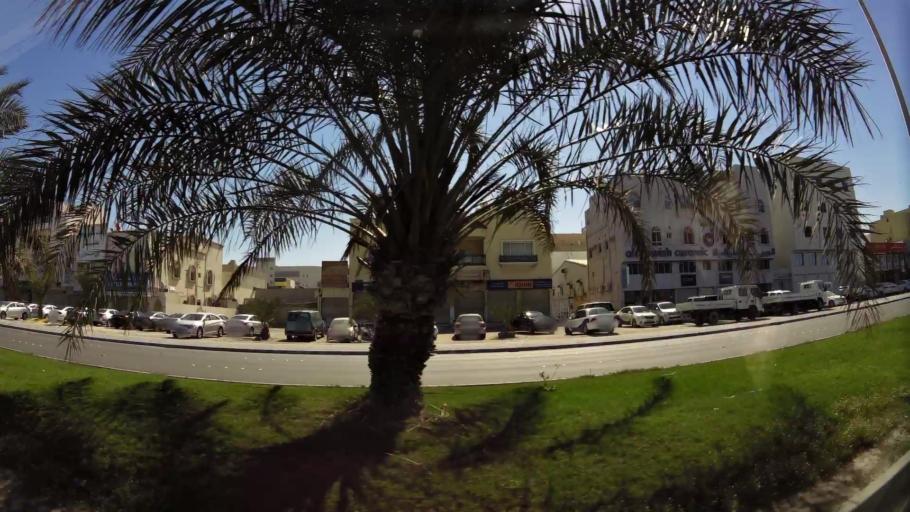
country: BH
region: Muharraq
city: Al Hadd
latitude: 26.2597
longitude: 50.6450
